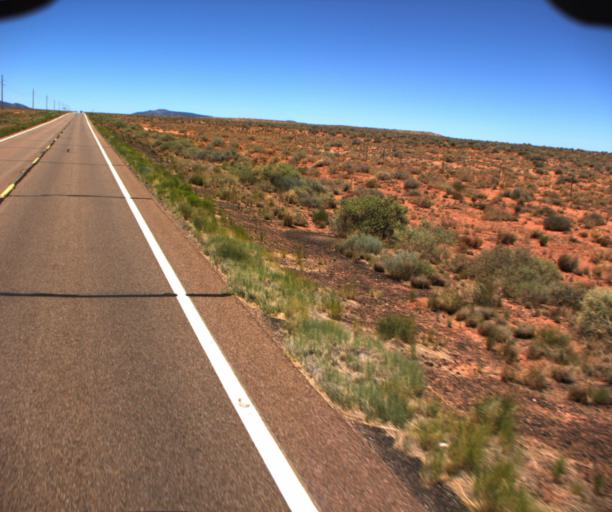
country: US
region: Arizona
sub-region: Coconino County
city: LeChee
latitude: 34.9491
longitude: -110.7648
